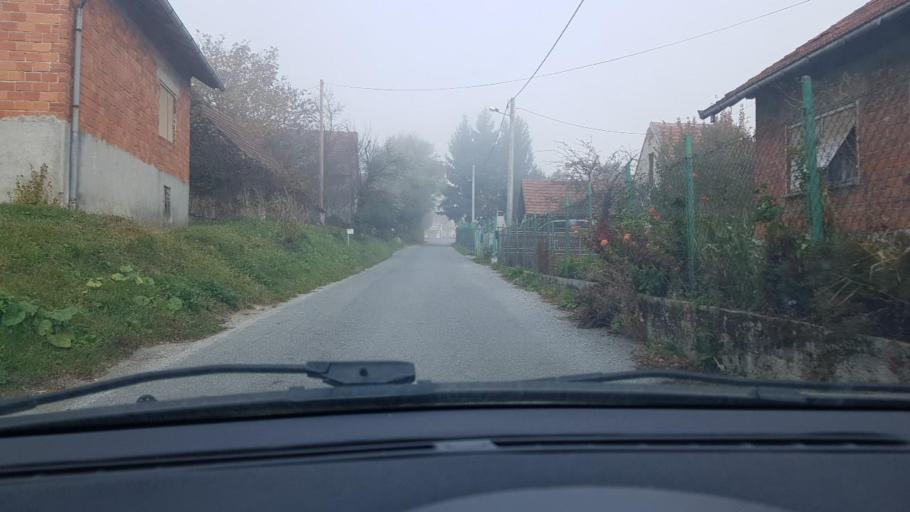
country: HR
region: Krapinsko-Zagorska
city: Mihovljan
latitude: 46.1552
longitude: 15.9898
